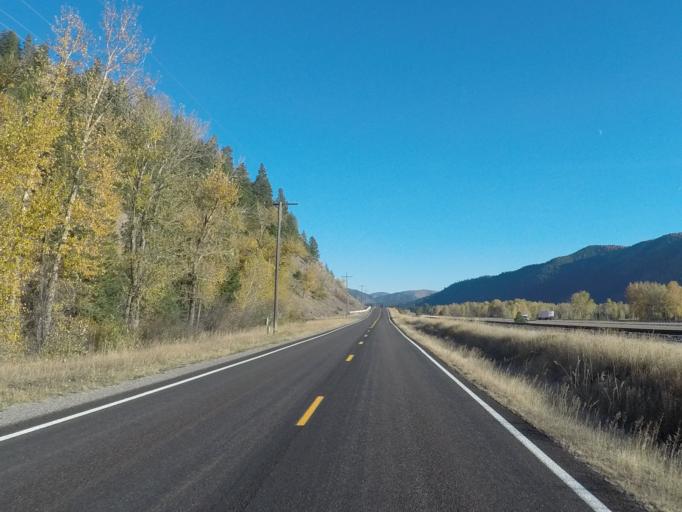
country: US
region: Montana
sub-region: Missoula County
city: Clinton
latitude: 46.8147
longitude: -113.7914
